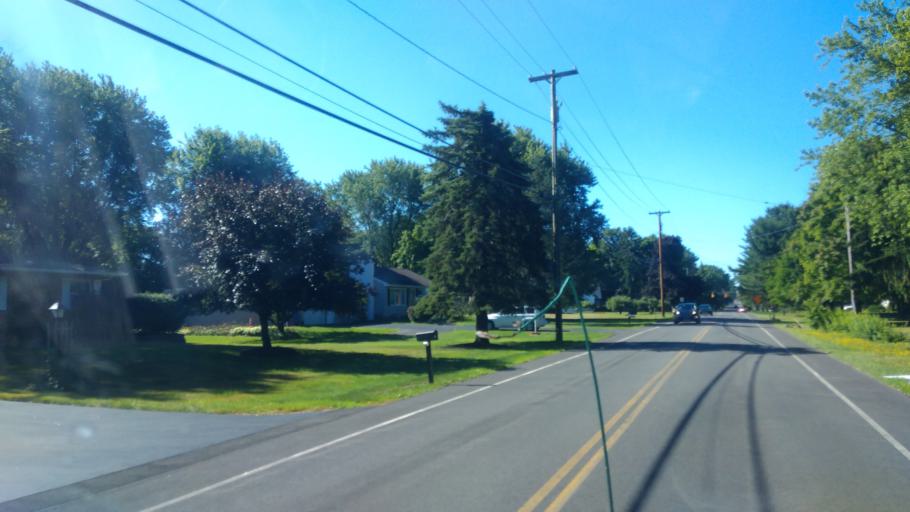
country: US
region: New York
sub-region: Monroe County
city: Webster
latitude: 43.2327
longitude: -77.4614
